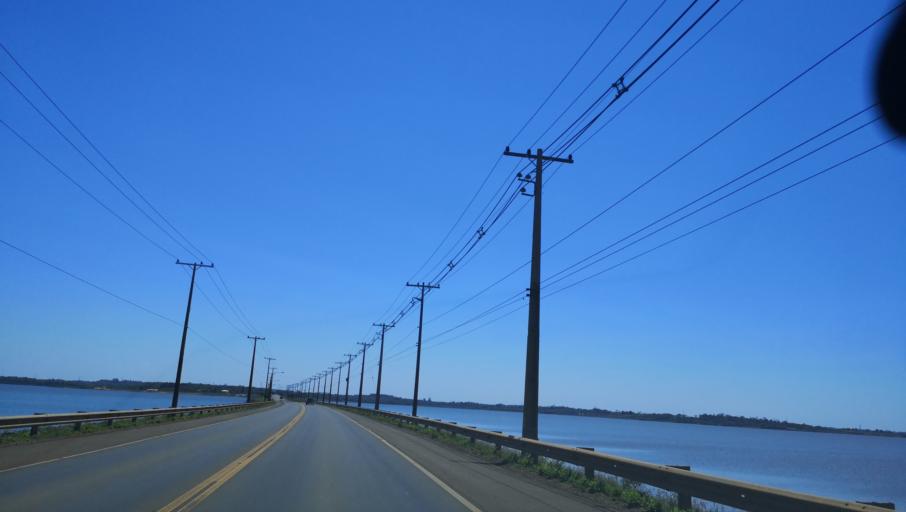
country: PY
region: Itapua
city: Carmen del Parana
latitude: -27.2084
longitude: -56.1623
